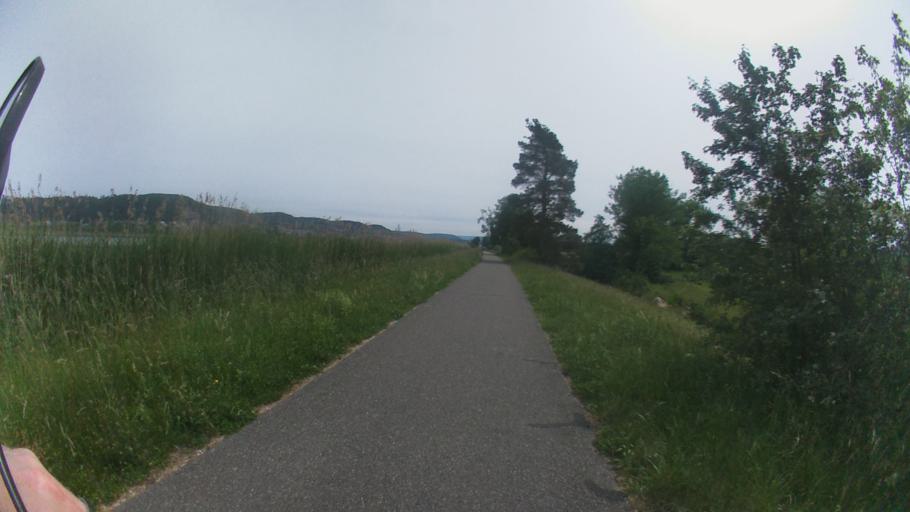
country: CH
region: Aargau
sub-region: Bezirk Zurzach
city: Klingnau
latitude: 47.5868
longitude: 8.2292
